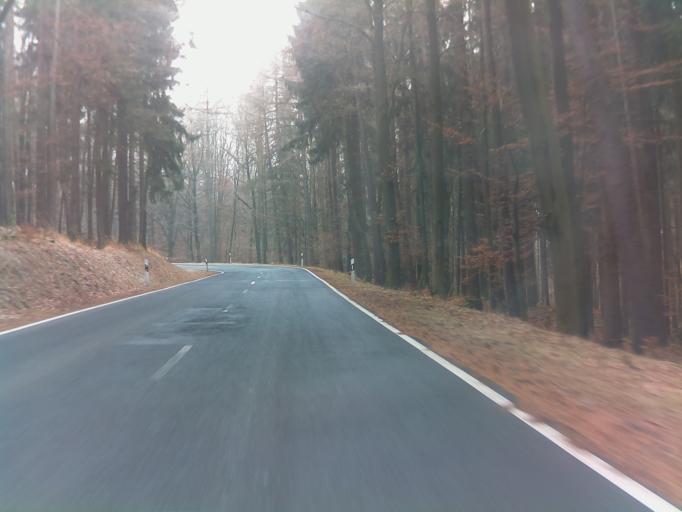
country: DE
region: Hesse
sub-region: Regierungsbezirk Darmstadt
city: Bad Orb
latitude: 50.1997
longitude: 9.4073
